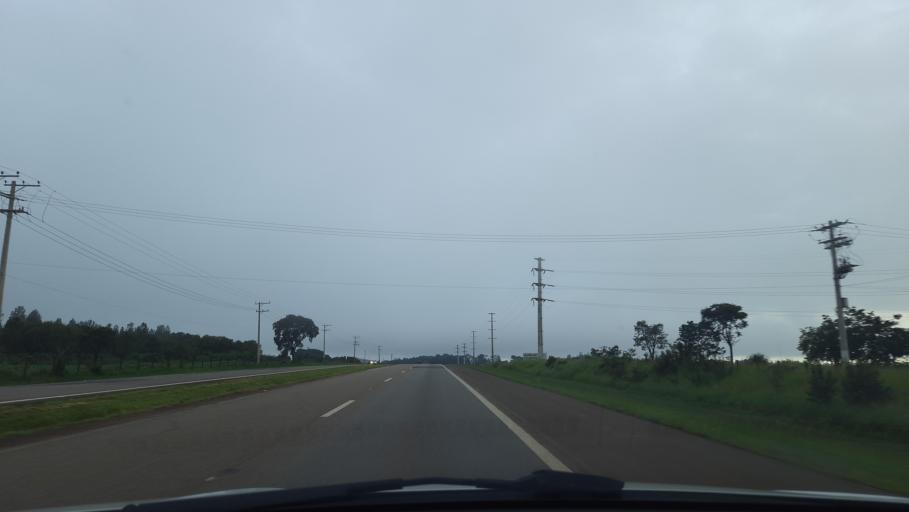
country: BR
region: Sao Paulo
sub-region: Casa Branca
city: Casa Branca
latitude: -21.7562
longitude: -47.0710
